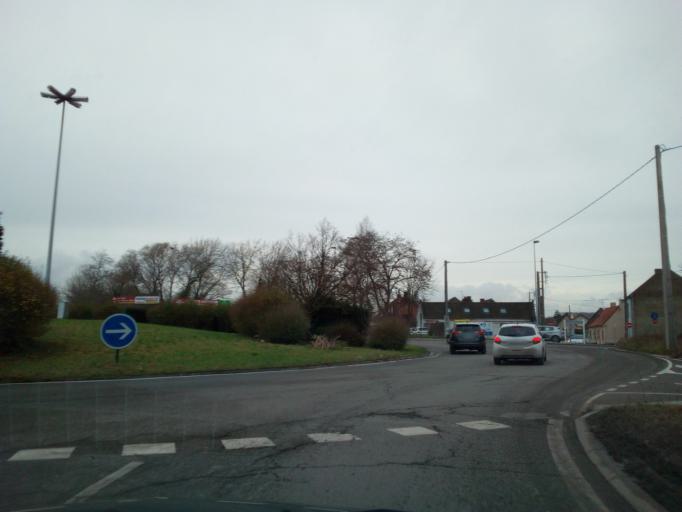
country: FR
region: Nord-Pas-de-Calais
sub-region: Departement du Pas-de-Calais
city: Beuvry
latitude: 50.5140
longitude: 2.6936
